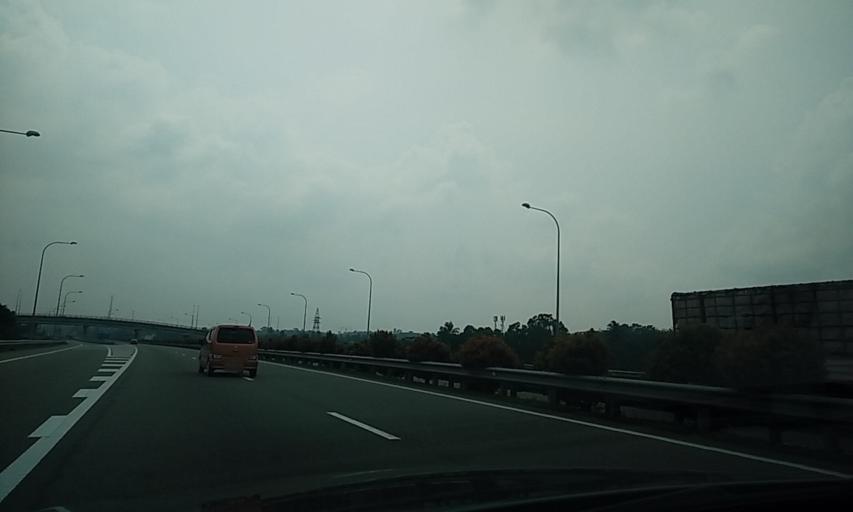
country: LK
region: Western
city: Homagama
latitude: 6.8872
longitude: 79.9768
